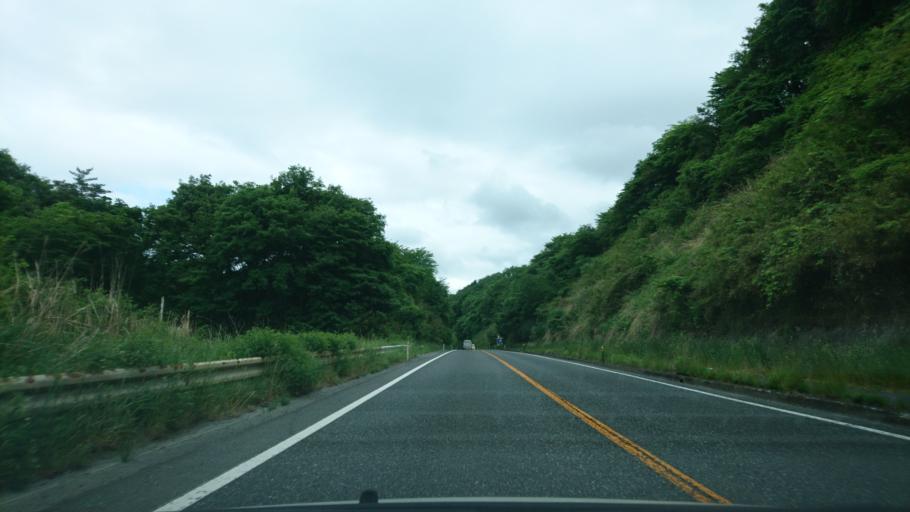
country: JP
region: Iwate
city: Ichinoseki
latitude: 38.8952
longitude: 141.1154
